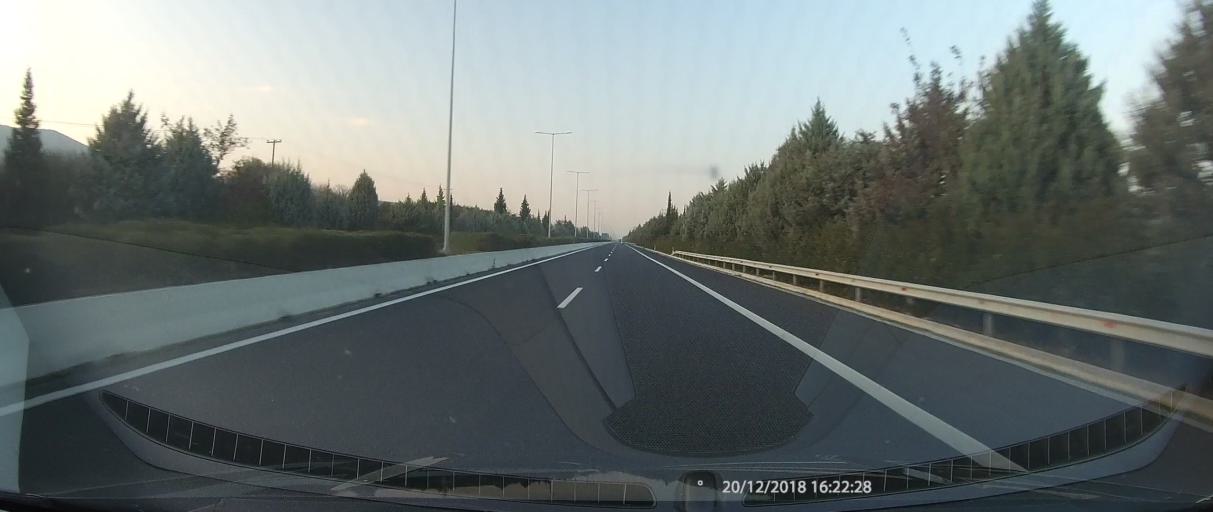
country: GR
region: Thessaly
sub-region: Nomos Magnisias
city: Sourpi
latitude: 39.0703
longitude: 22.8862
